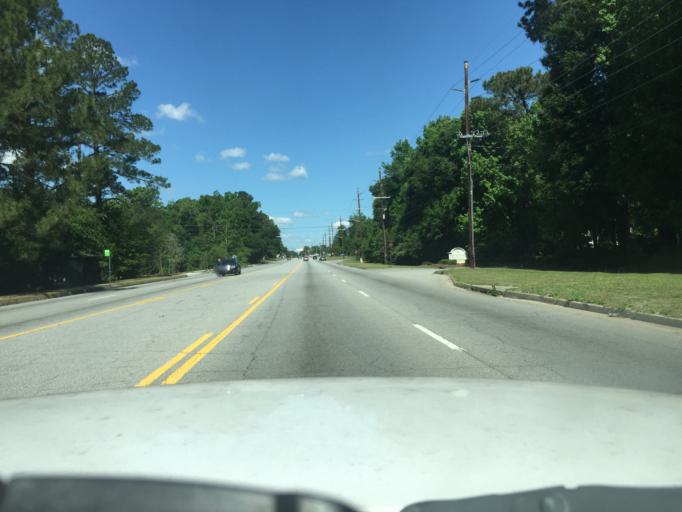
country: US
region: Georgia
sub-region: Chatham County
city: Isle of Hope
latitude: 32.0040
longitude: -81.0912
